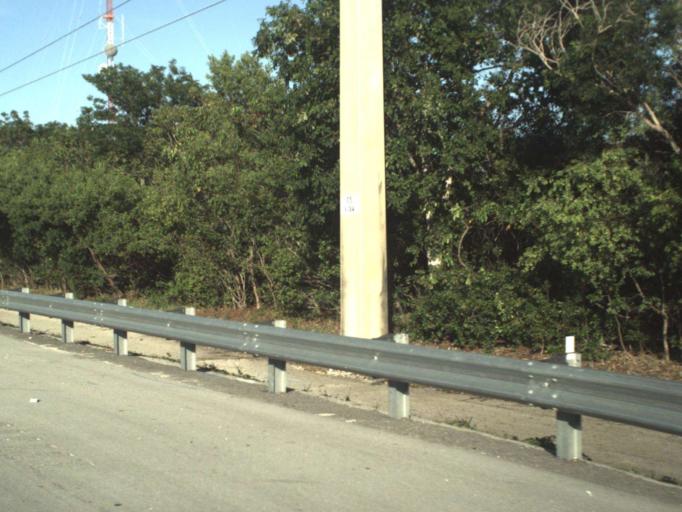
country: US
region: Florida
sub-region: Monroe County
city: Islamorada
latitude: 24.8210
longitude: -80.8201
